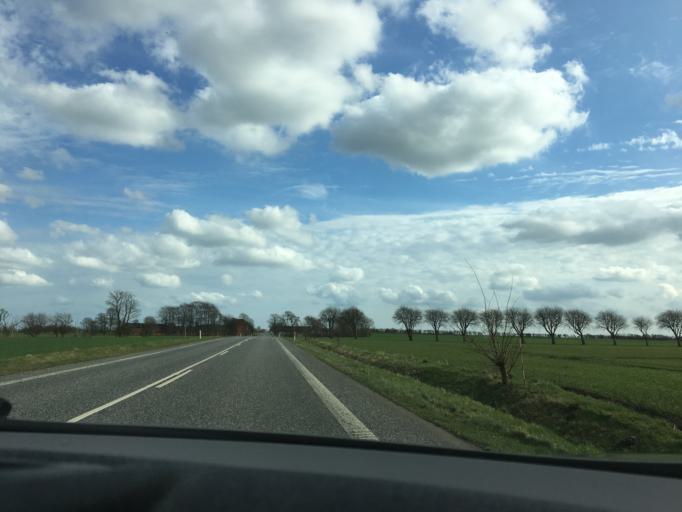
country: DK
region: South Denmark
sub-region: Vejle Kommune
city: Jelling
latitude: 55.7657
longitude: 9.4037
